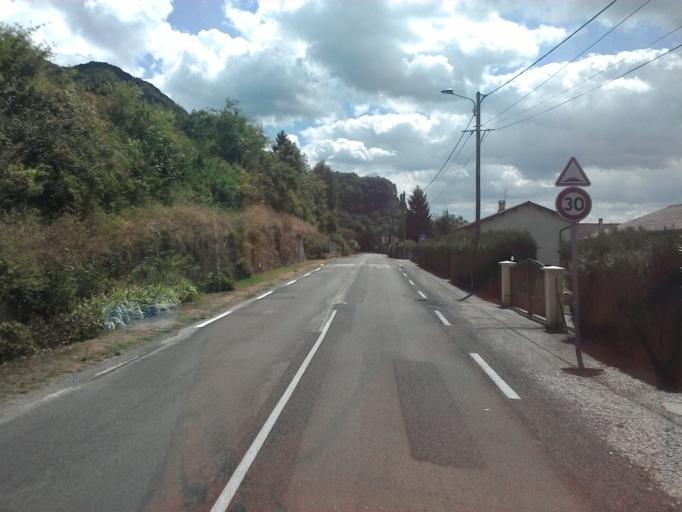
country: FR
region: Rhone-Alpes
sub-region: Departement de l'Ain
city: Saint-Sorlin-en-Bugey
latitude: 45.8900
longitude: 5.3649
